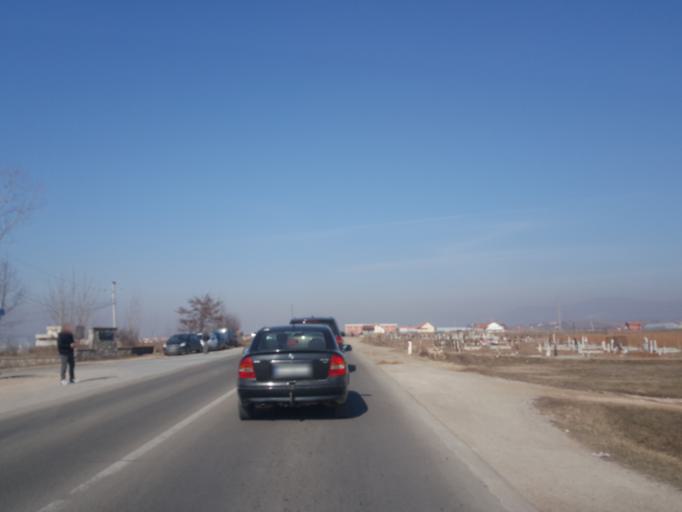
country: XK
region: Mitrovica
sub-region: Vushtrri
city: Vushtrri
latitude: 42.7868
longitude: 21.0080
